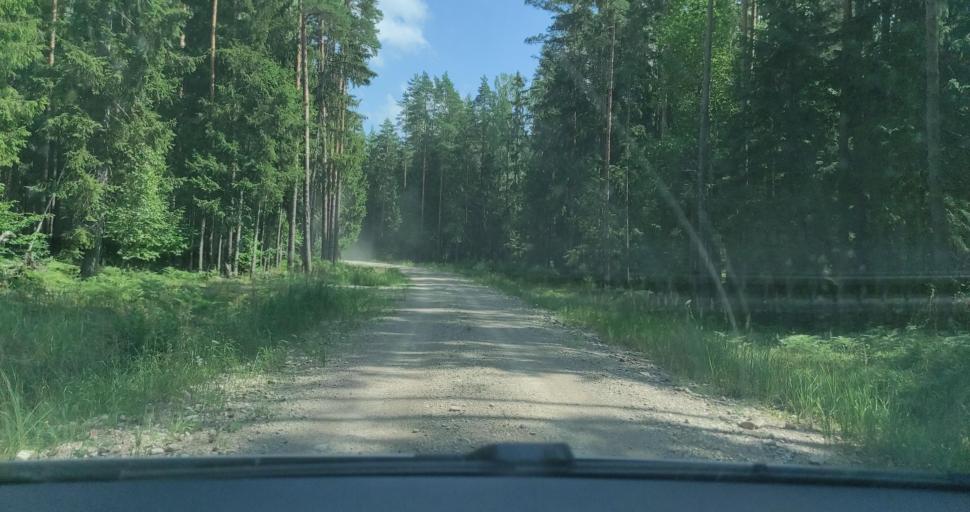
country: LV
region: Kuldigas Rajons
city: Kuldiga
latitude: 57.0677
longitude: 22.1987
